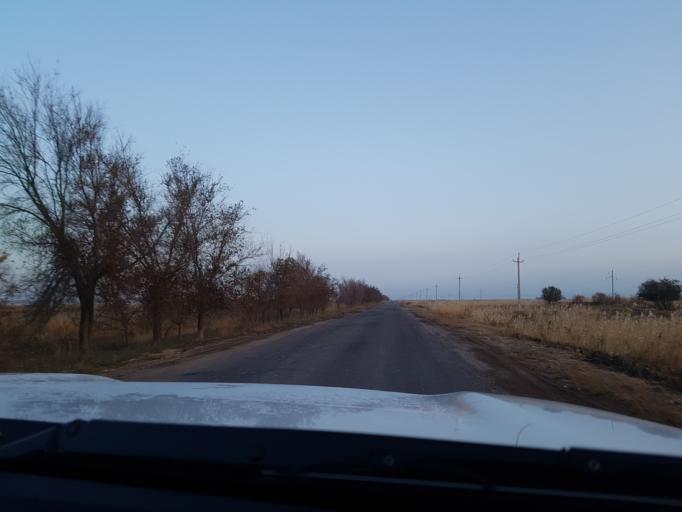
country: TM
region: Dasoguz
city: Koeneuergench
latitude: 41.7603
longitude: 58.6917
